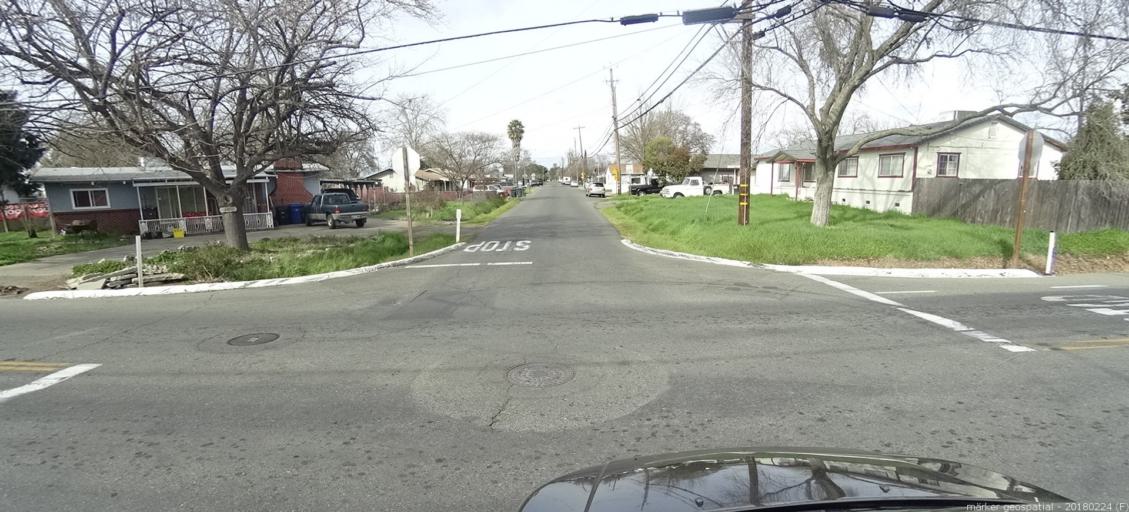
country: US
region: California
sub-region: Sacramento County
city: Rio Linda
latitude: 38.6983
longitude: -121.4476
